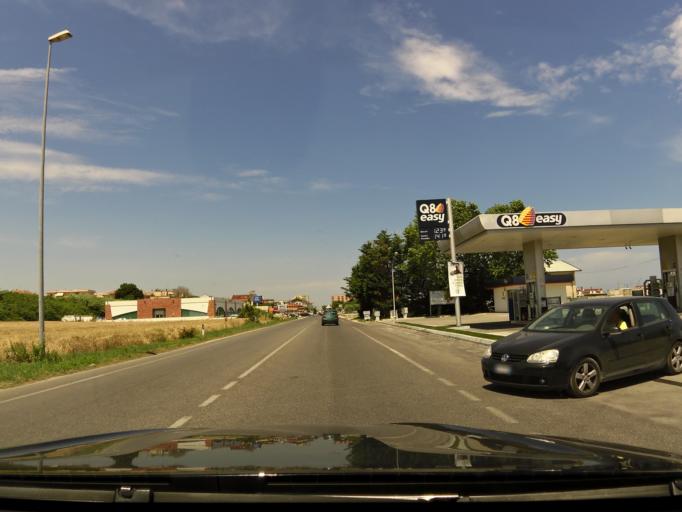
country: IT
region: The Marches
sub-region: Provincia di Pesaro e Urbino
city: Marotta
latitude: 43.7565
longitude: 13.1577
